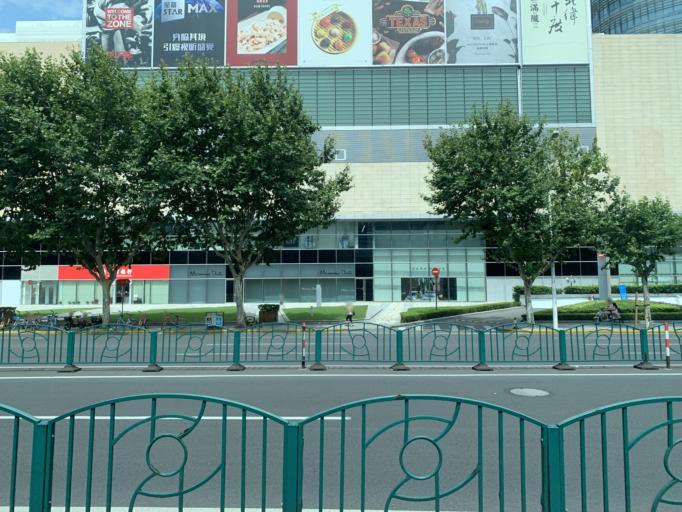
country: CN
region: Shanghai Shi
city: Pudong
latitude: 31.2292
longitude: 121.5217
